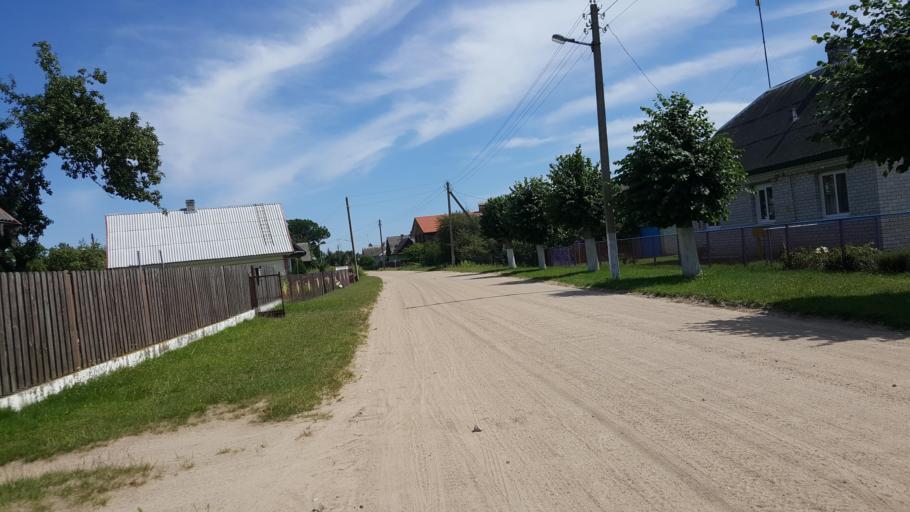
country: BY
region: Brest
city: Pruzhany
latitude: 52.5620
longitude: 24.2084
